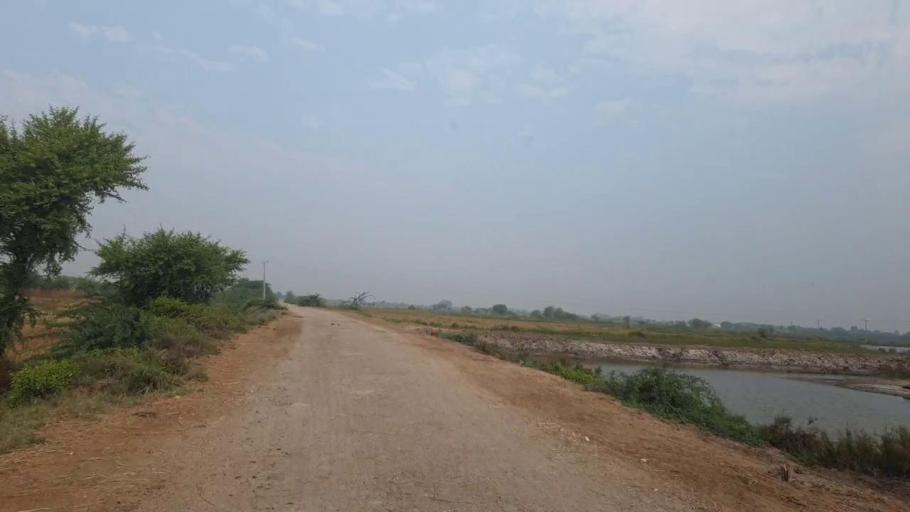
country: PK
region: Sindh
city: Tando Bago
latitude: 24.7860
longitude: 68.8867
